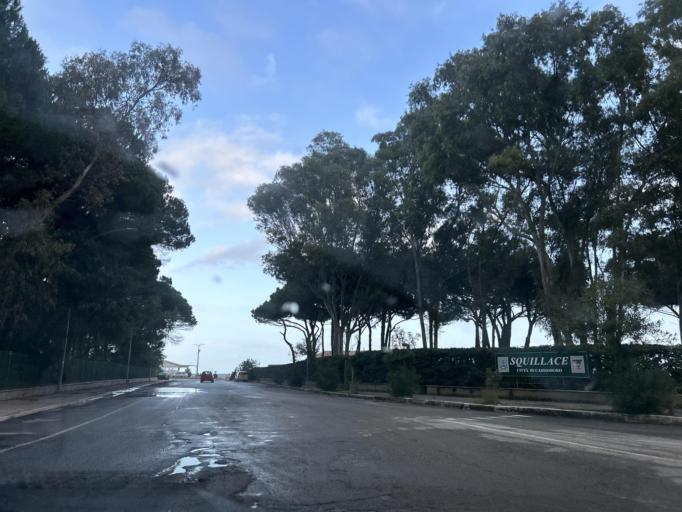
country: IT
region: Calabria
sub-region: Provincia di Catanzaro
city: Squillace Lido
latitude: 38.7776
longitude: 16.5742
